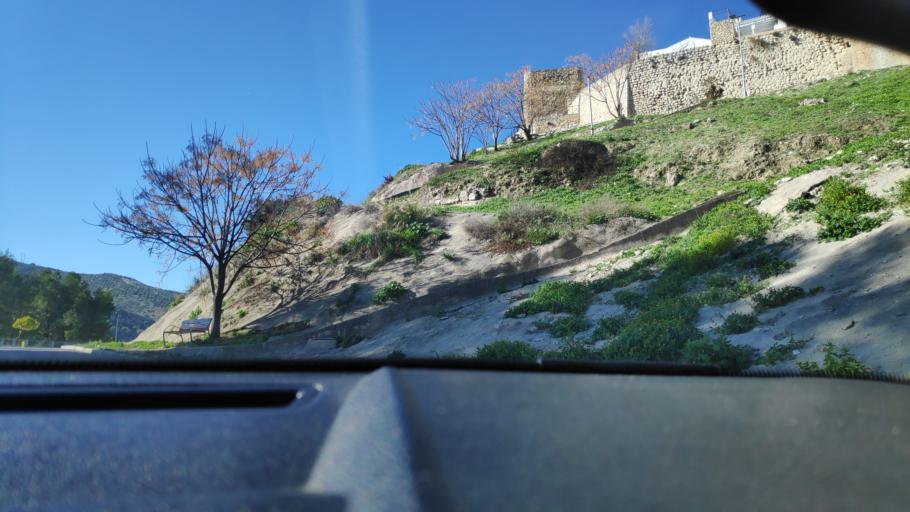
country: ES
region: Andalusia
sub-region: Province of Cordoba
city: Baena
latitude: 37.6120
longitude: -4.3271
